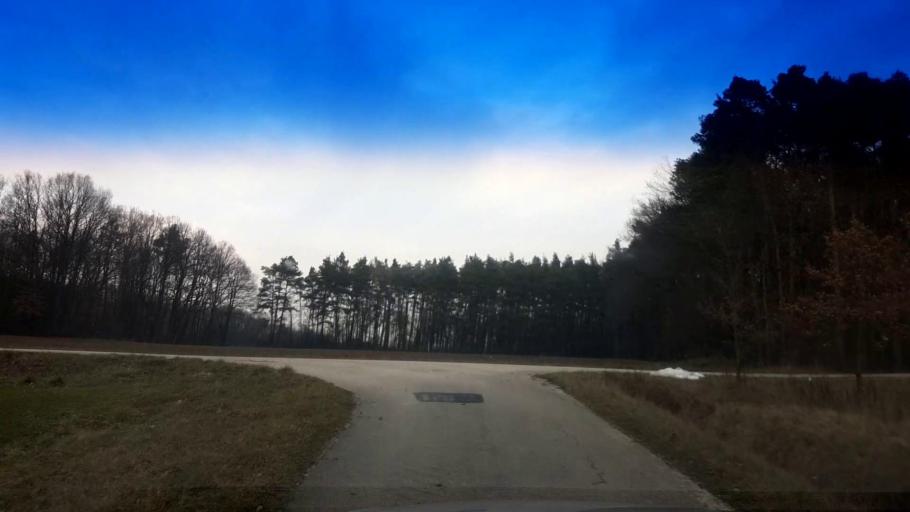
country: DE
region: Bavaria
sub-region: Upper Franconia
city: Hallerndorf
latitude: 49.7799
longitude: 10.9774
